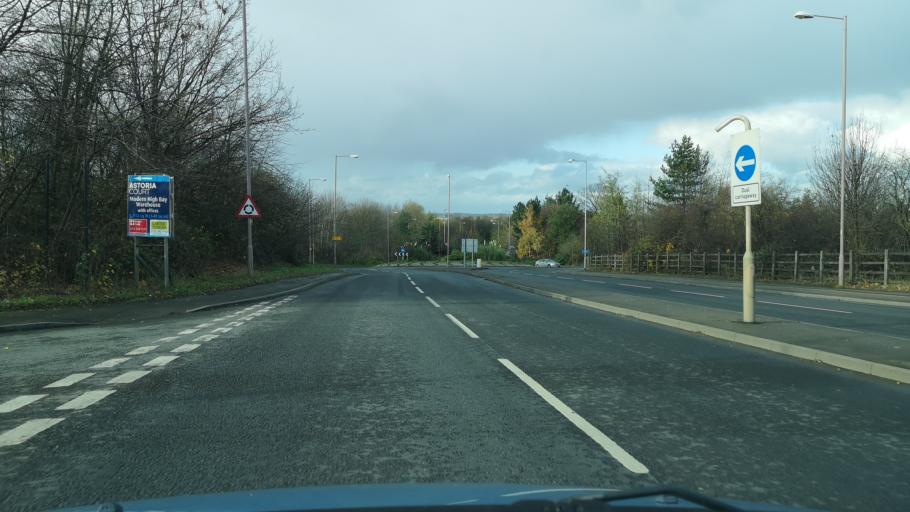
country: GB
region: England
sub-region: City and Borough of Wakefield
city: Normanton
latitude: 53.7001
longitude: -1.3922
